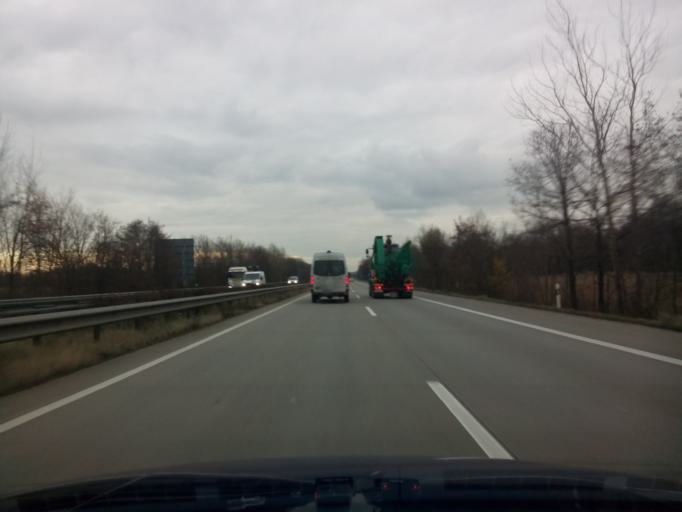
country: DE
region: Lower Saxony
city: Loxstedt
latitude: 53.4914
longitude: 8.6245
